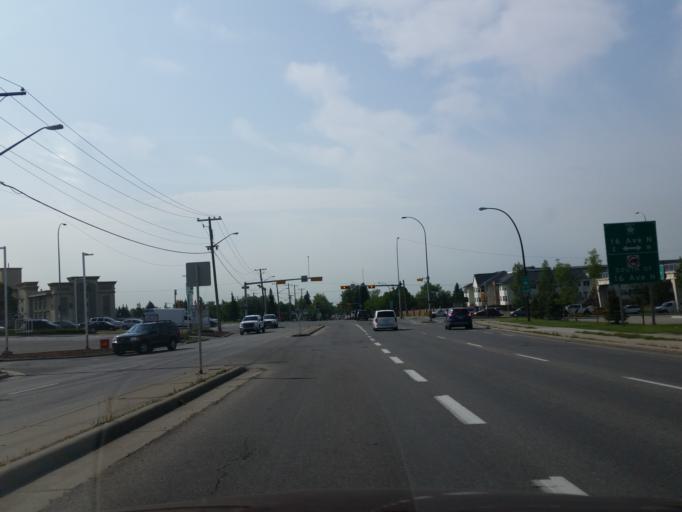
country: CA
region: Alberta
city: Calgary
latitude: 51.0681
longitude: -114.0134
